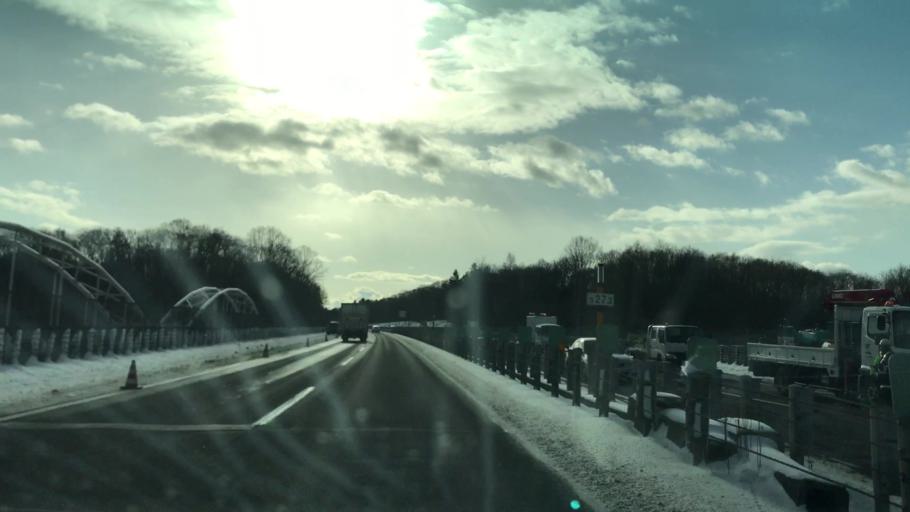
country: JP
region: Hokkaido
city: Chitose
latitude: 42.8627
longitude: 141.5584
